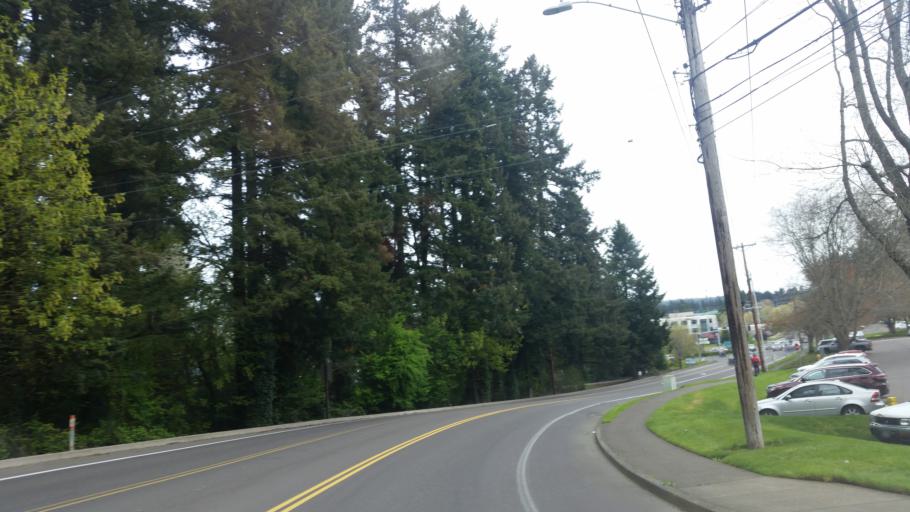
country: US
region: Oregon
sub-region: Washington County
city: Durham
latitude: 45.4009
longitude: -122.7542
